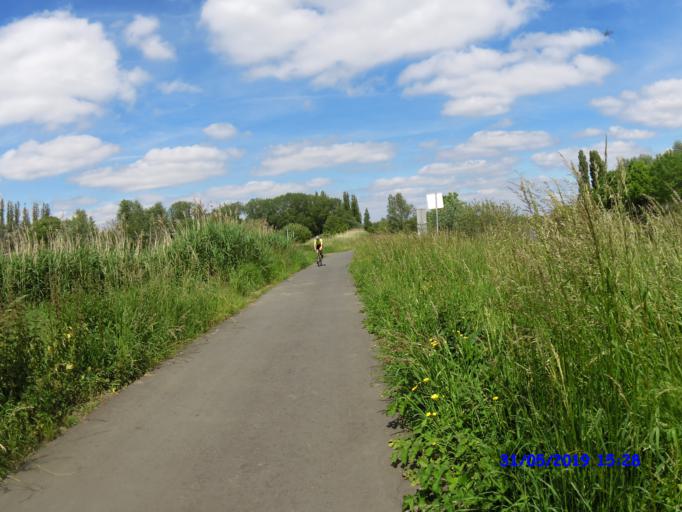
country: FR
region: Nord-Pas-de-Calais
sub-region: Departement du Nord
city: Comines
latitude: 50.7719
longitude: 3.0153
